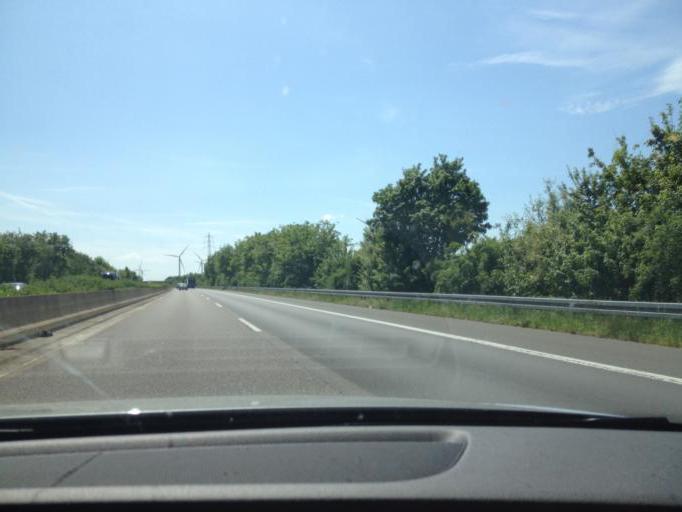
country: DE
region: North Rhine-Westphalia
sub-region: Regierungsbezirk Koln
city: Weilerswist
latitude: 50.7261
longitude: 6.7841
